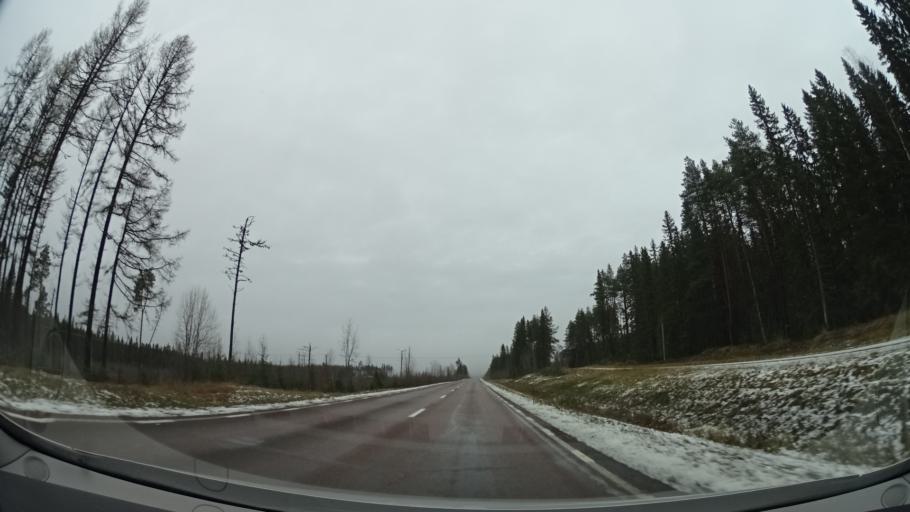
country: SE
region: Vaesterbotten
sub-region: Dorotea Kommun
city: Dorotea
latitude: 64.1742
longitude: 16.2907
